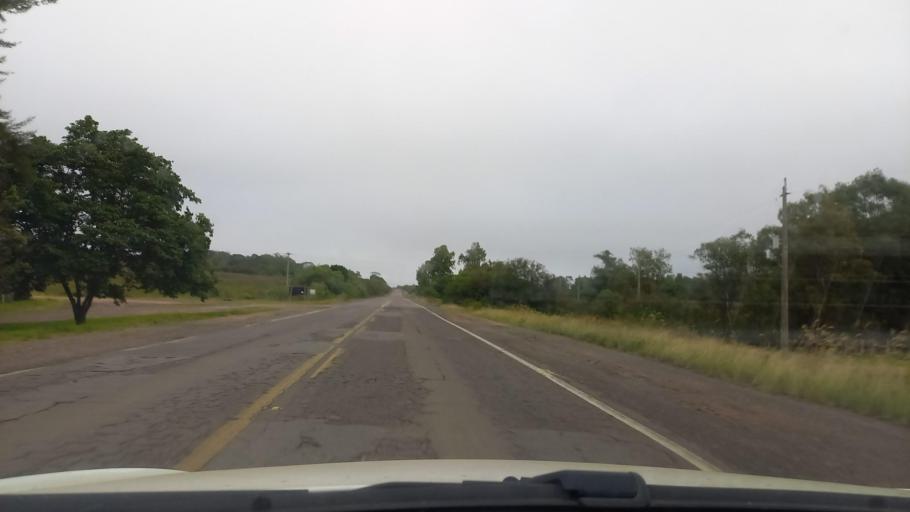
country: BR
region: Rio Grande do Sul
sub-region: Cacequi
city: Cacequi
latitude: -30.1224
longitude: -54.6421
